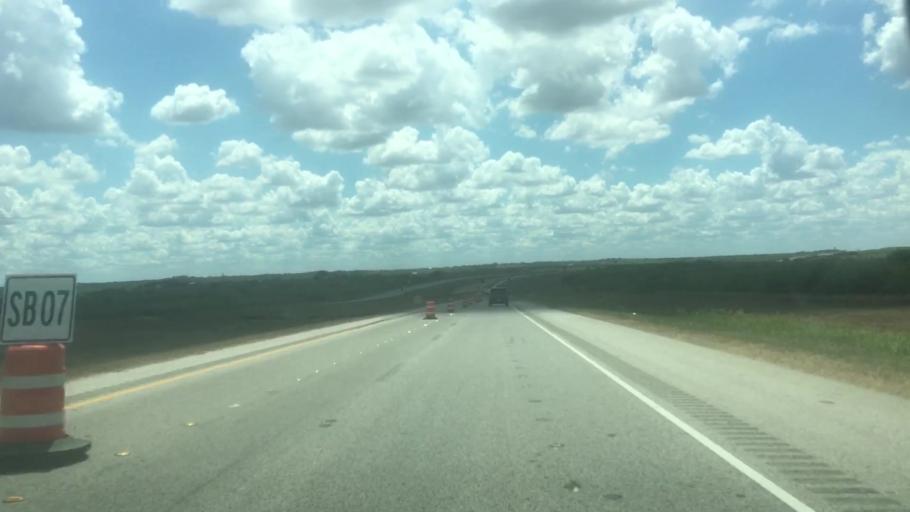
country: US
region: Texas
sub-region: Caldwell County
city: Lockhart
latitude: 29.8454
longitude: -97.7274
